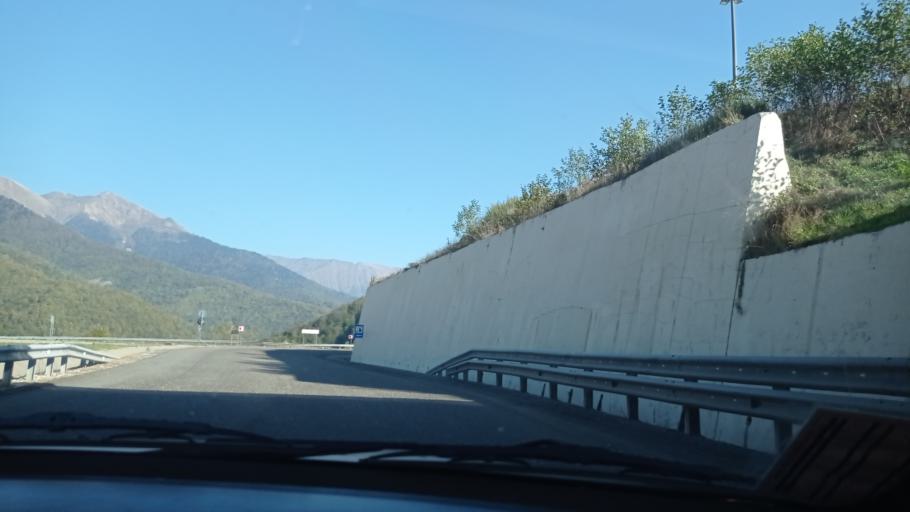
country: RU
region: Krasnodarskiy
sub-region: Sochi City
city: Krasnaya Polyana
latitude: 43.6709
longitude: 40.2877
